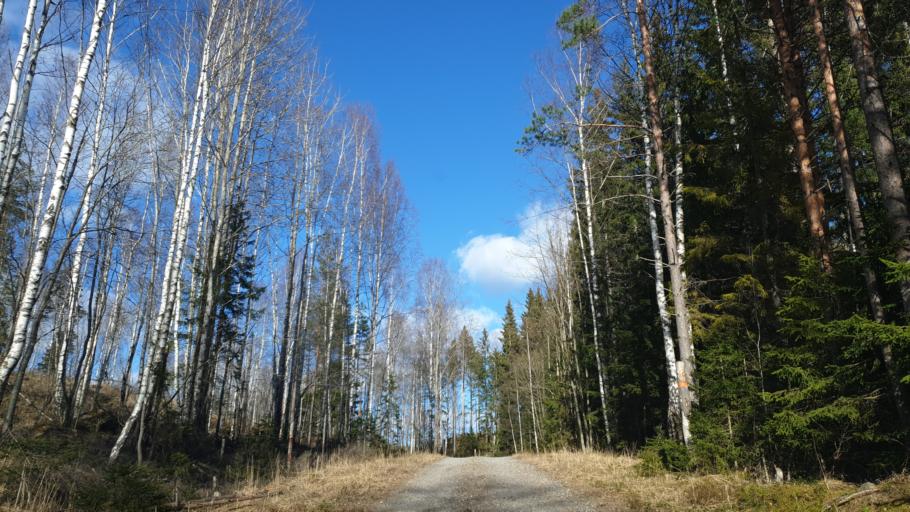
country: SE
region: OErebro
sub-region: Orebro Kommun
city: Garphyttan
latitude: 59.3734
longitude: 14.9755
